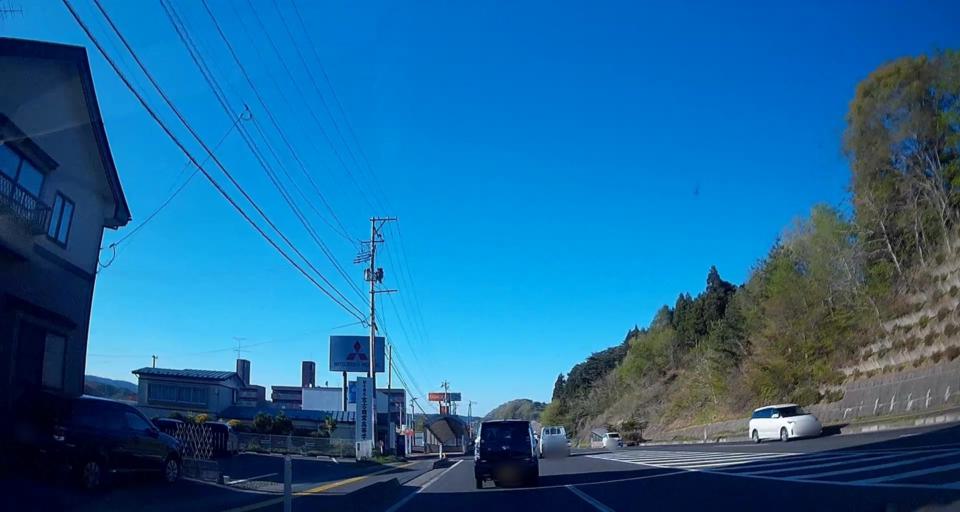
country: JP
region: Iwate
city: Miyako
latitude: 39.6174
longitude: 141.9611
